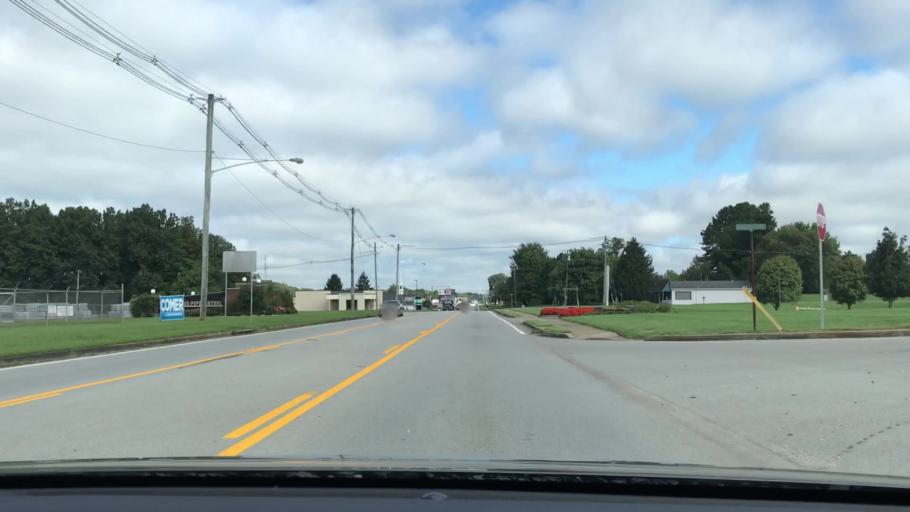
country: US
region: Kentucky
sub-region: Russell County
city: Jamestown
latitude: 37.0125
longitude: -85.0755
